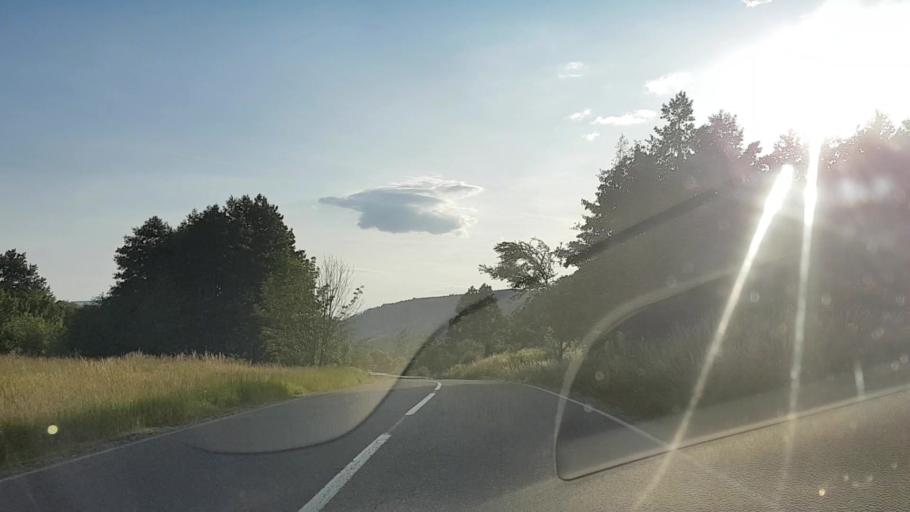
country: RO
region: Harghita
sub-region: Comuna Praid
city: Ocna de Sus
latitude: 46.5711
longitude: 25.1849
